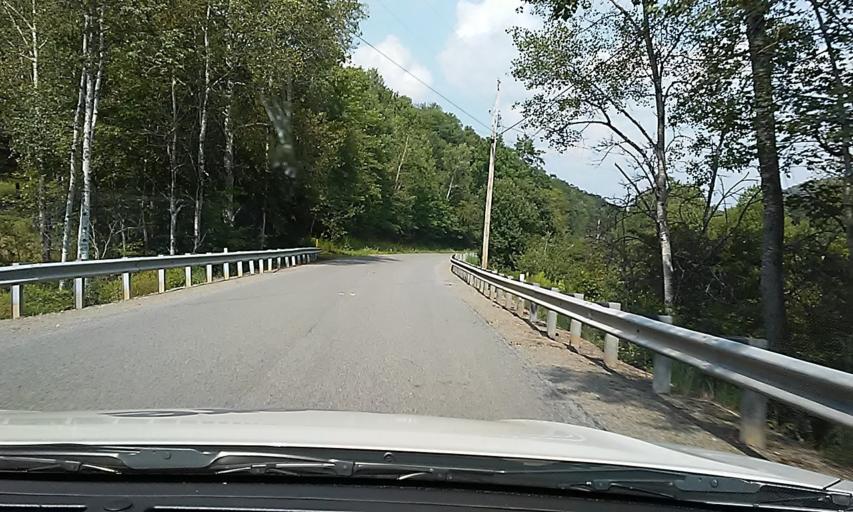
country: US
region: Pennsylvania
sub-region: Potter County
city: Coudersport
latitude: 41.8210
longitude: -77.8322
